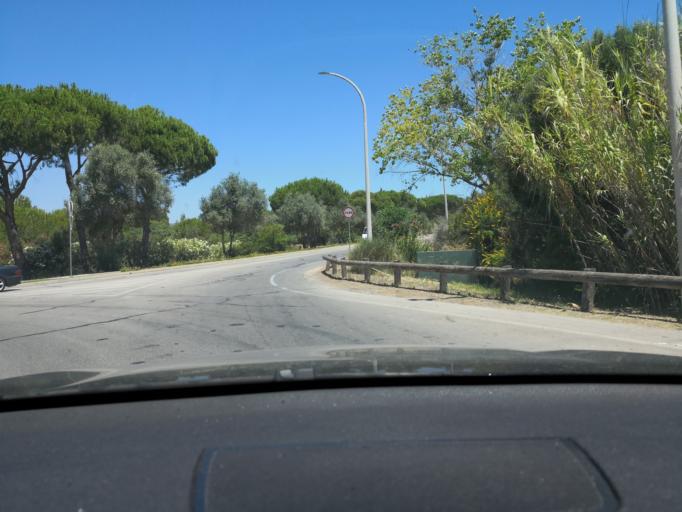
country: PT
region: Faro
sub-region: Loule
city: Vilamoura
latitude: 37.1026
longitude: -8.1241
